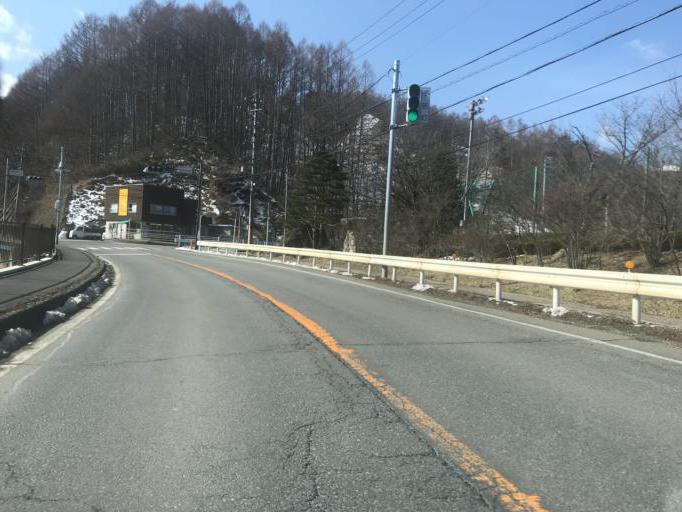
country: JP
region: Nagano
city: Saku
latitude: 36.0162
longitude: 138.4907
